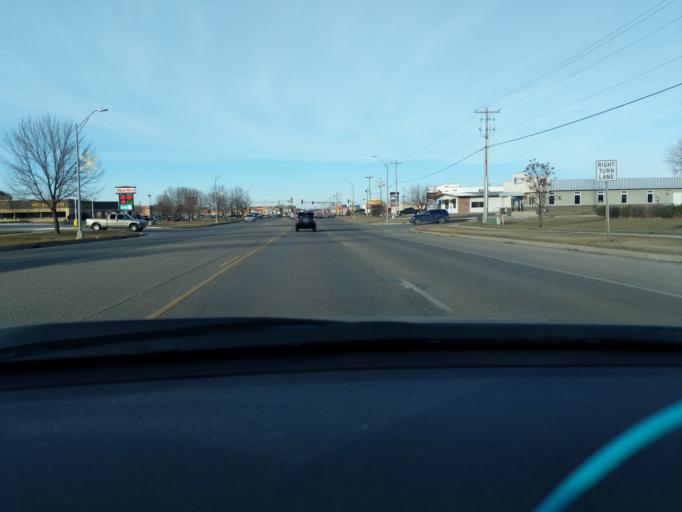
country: US
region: Minnesota
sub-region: Kandiyohi County
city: Willmar
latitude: 45.1014
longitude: -95.0426
